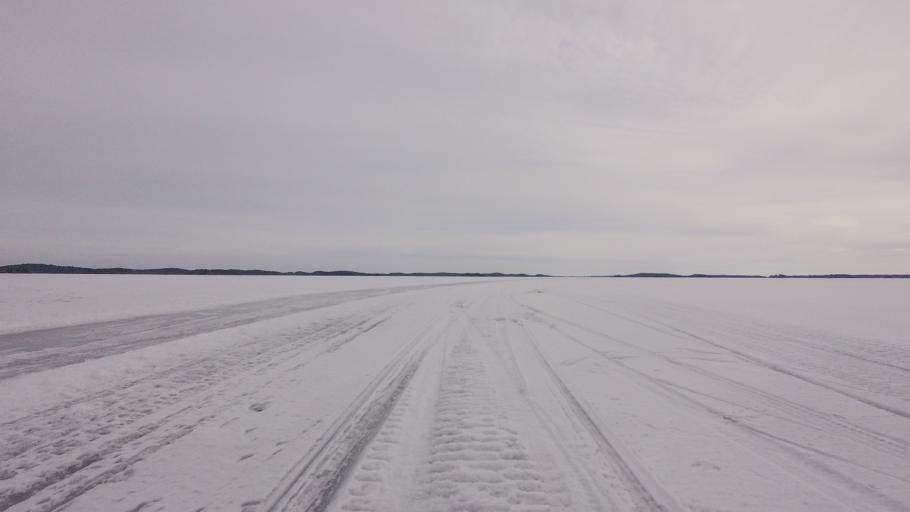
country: FI
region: Southern Savonia
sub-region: Savonlinna
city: Rantasalmi
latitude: 62.1134
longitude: 28.3771
